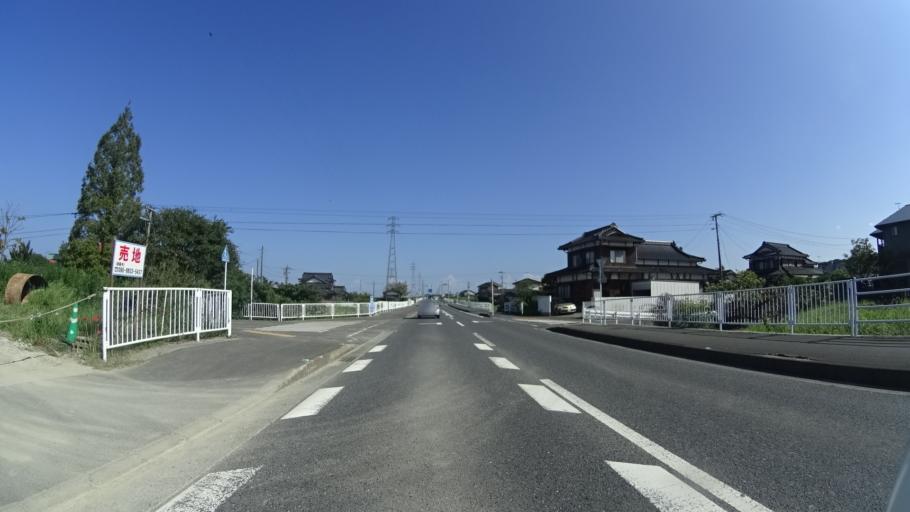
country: JP
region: Fukuoka
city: Shiida
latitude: 33.6493
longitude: 131.0549
